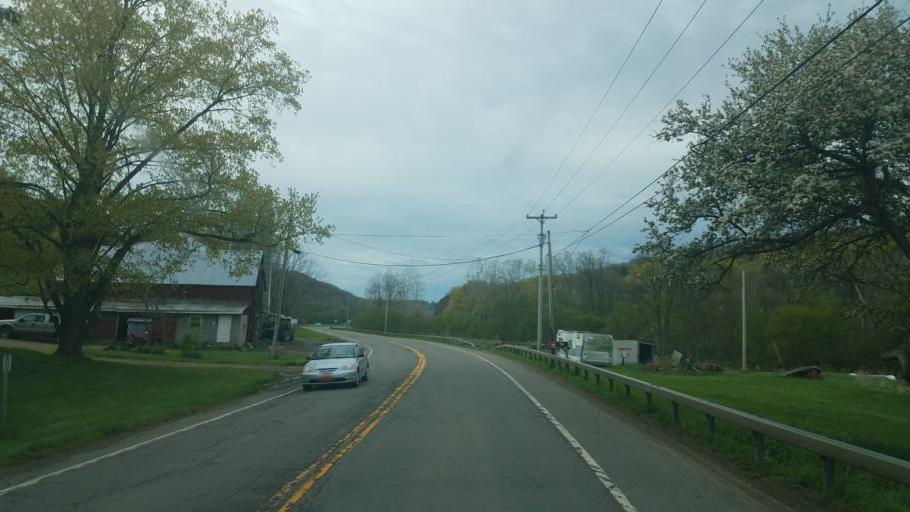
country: US
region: New York
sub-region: Steuben County
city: Canisteo
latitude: 42.2145
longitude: -77.5689
